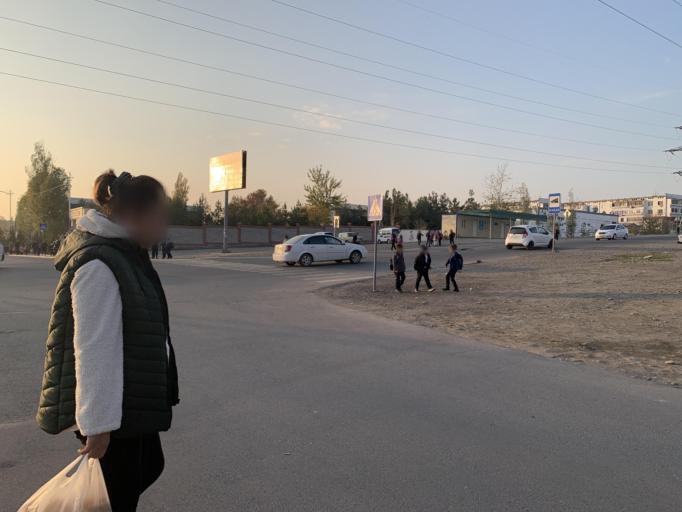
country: UZ
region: Namangan
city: Namangan Shahri
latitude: 41.0025
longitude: 71.6038
